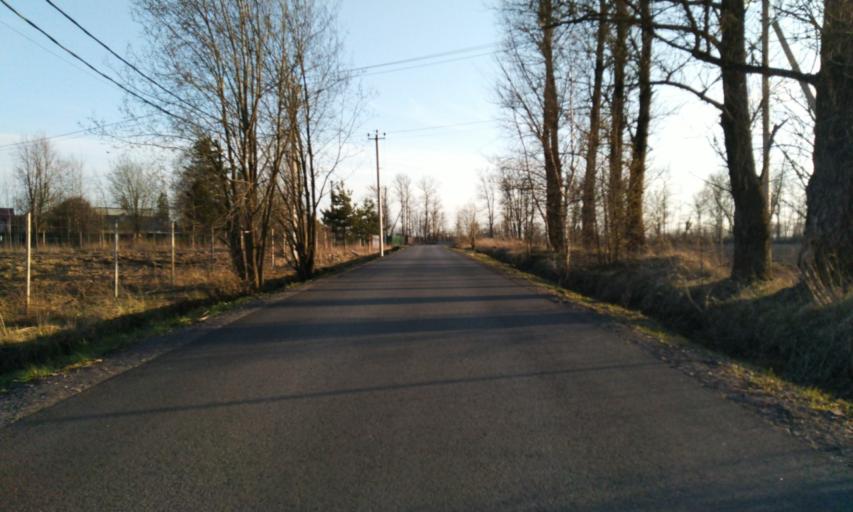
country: RU
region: Leningrad
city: Novoye Devyatkino
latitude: 60.1033
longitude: 30.4488
